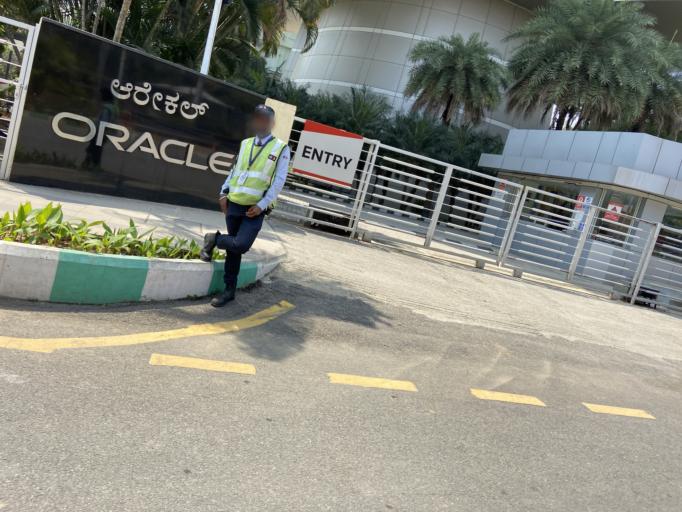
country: IN
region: Karnataka
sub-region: Bangalore Urban
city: Bangalore
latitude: 12.9797
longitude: 77.6570
